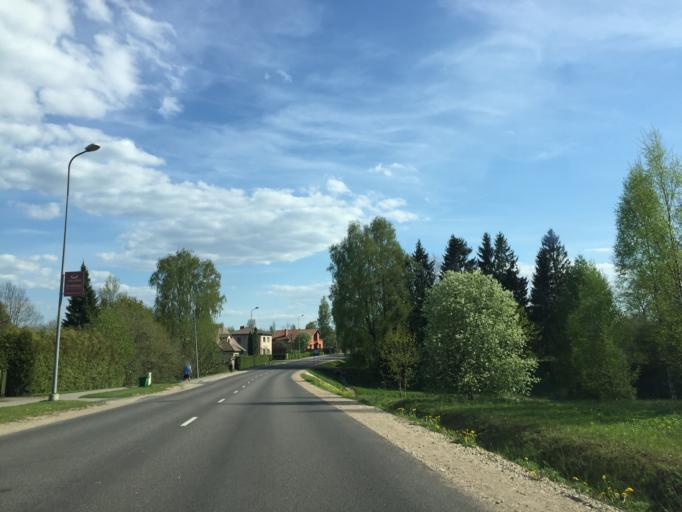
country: LV
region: Limbazu Rajons
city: Limbazi
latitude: 57.5041
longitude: 24.7159
